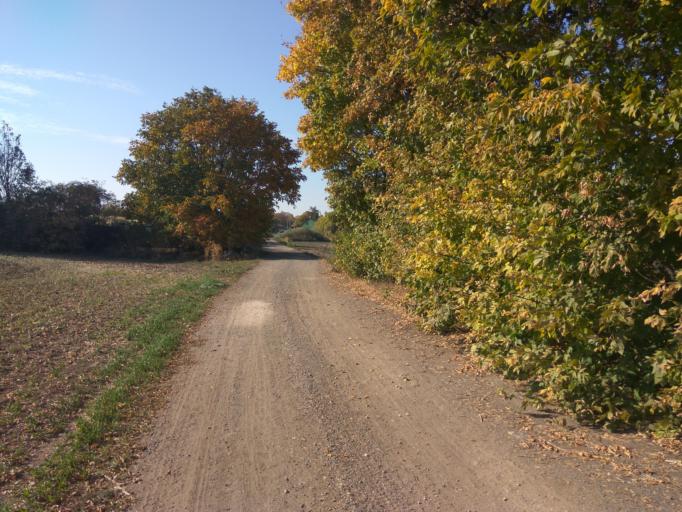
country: CZ
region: Central Bohemia
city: Hovorcovice
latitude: 50.1772
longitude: 14.5292
